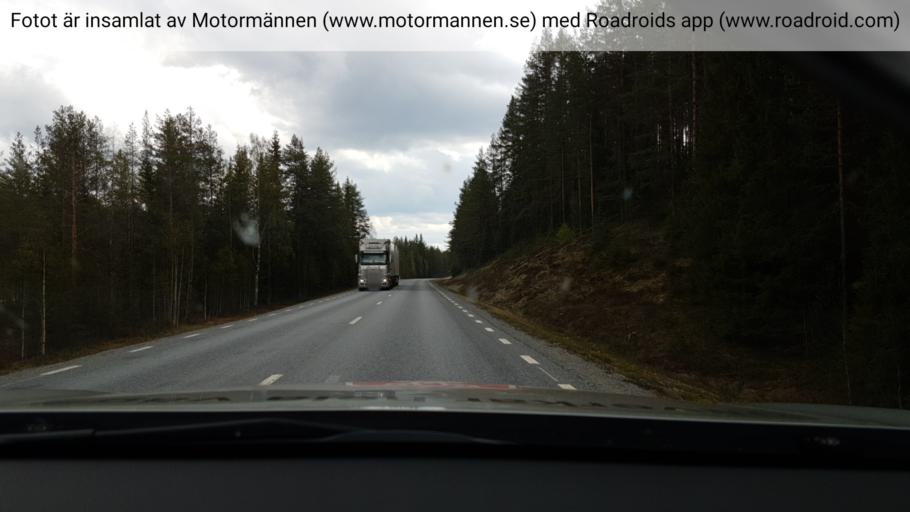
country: SE
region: Vaesterbotten
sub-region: Bjurholms Kommun
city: Bjurholm
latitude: 63.9853
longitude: 18.8053
